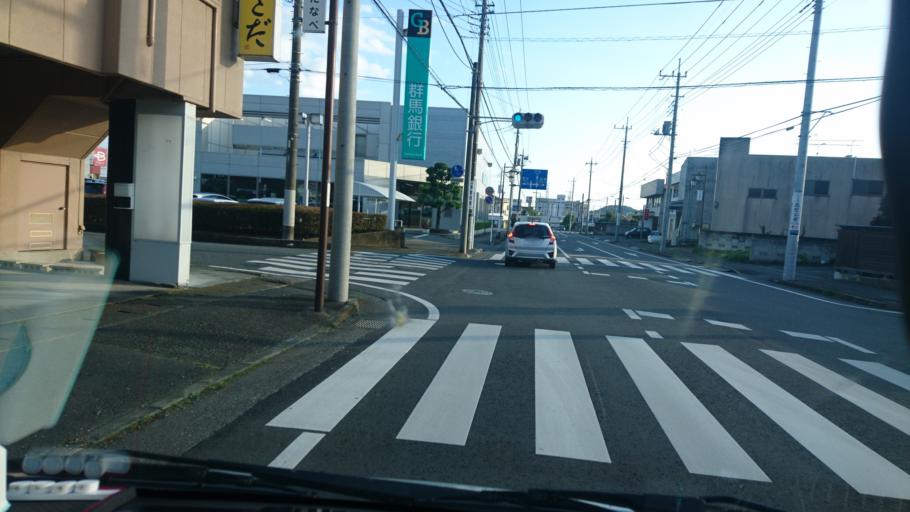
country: JP
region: Gunma
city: Omamacho-omama
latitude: 36.4302
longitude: 139.2772
